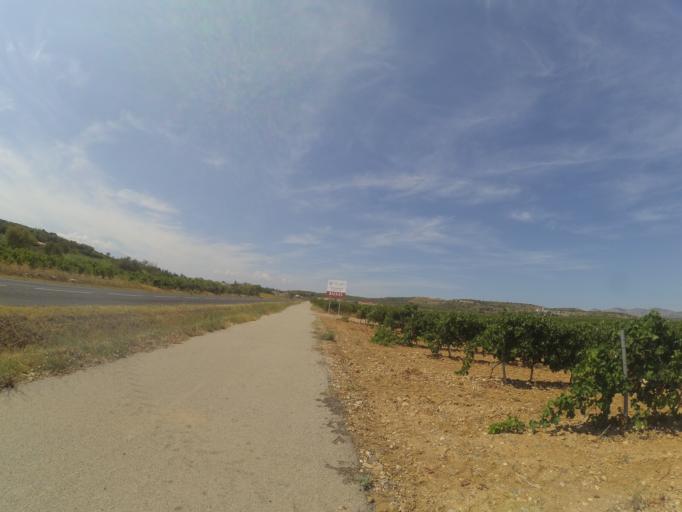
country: FR
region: Languedoc-Roussillon
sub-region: Departement des Pyrenees-Orientales
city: Baixas
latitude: 42.7545
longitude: 2.8241
